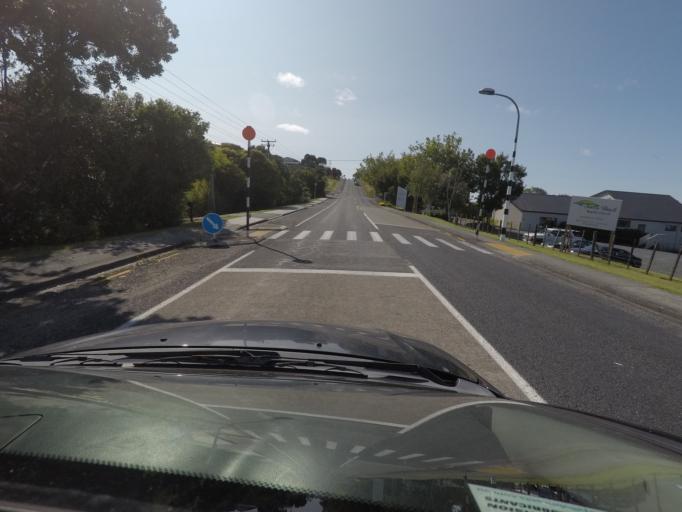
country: NZ
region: Auckland
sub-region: Auckland
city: Warkworth
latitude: -36.4273
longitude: 174.7309
